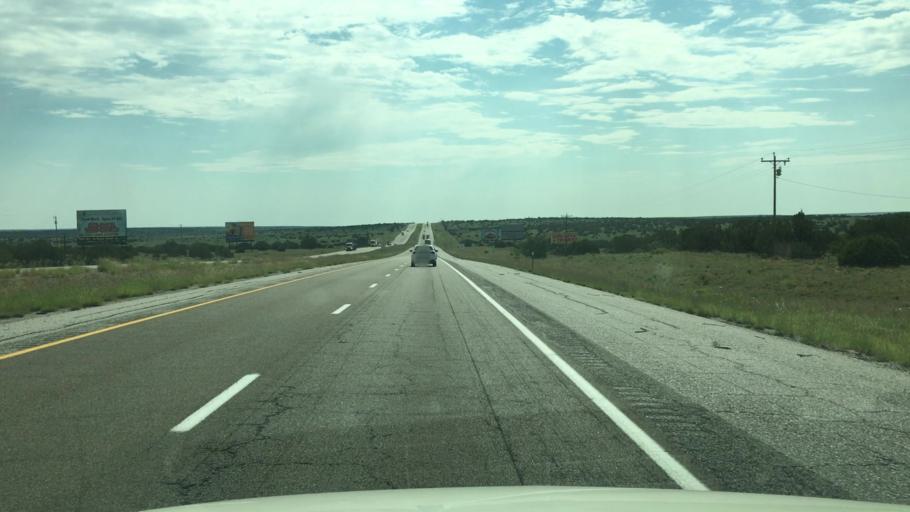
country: US
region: New Mexico
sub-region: Torrance County
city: Moriarty
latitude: 34.9983
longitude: -105.4386
